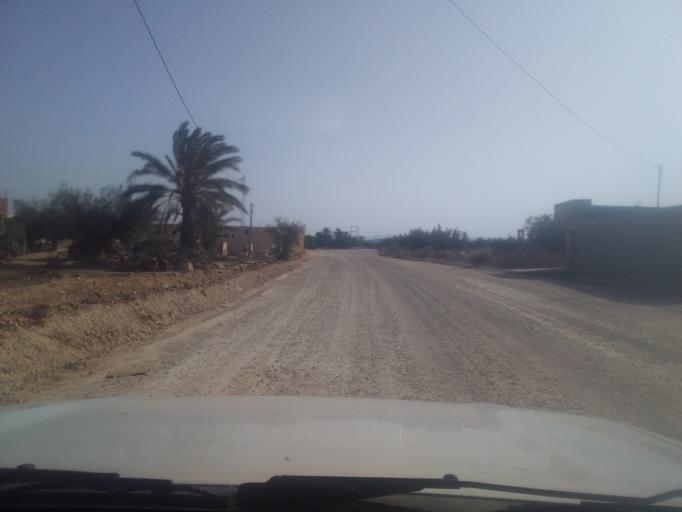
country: TN
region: Qabis
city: Matmata
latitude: 33.6036
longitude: 10.2776
